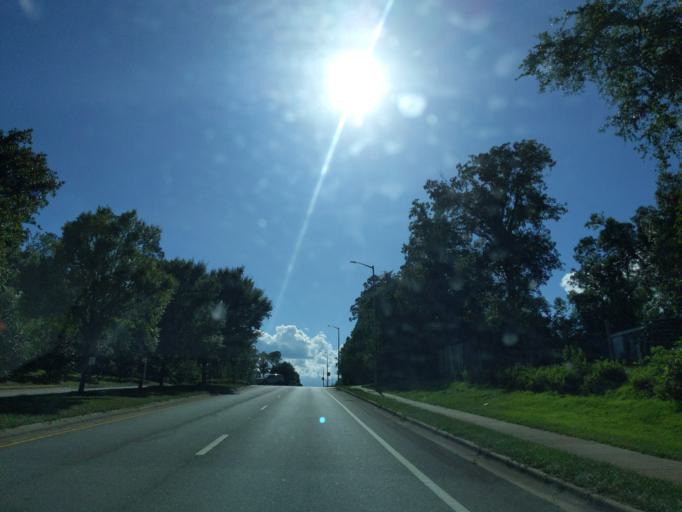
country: US
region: Florida
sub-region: Leon County
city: Tallahassee
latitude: 30.4108
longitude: -84.2430
